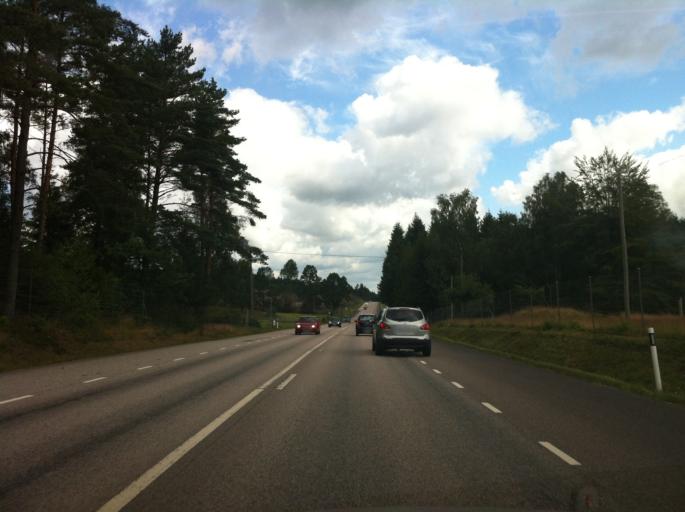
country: SE
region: Halland
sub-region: Halmstads Kommun
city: Oskarstrom
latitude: 56.7758
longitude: 12.9522
